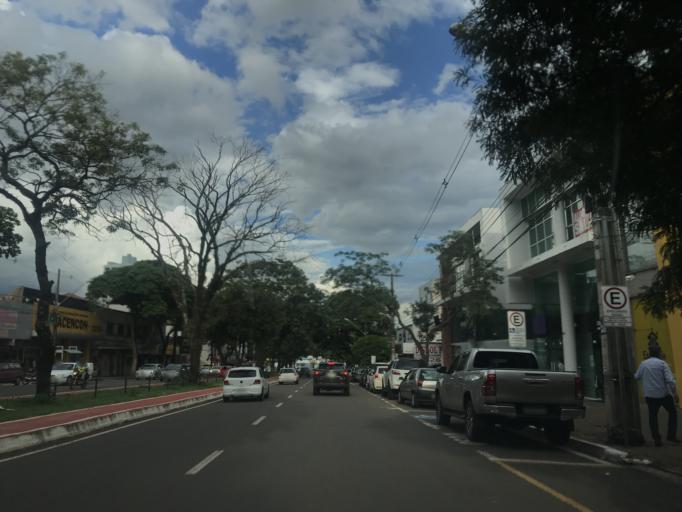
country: BR
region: Parana
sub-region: Maringa
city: Maringa
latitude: -23.4216
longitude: -51.9495
